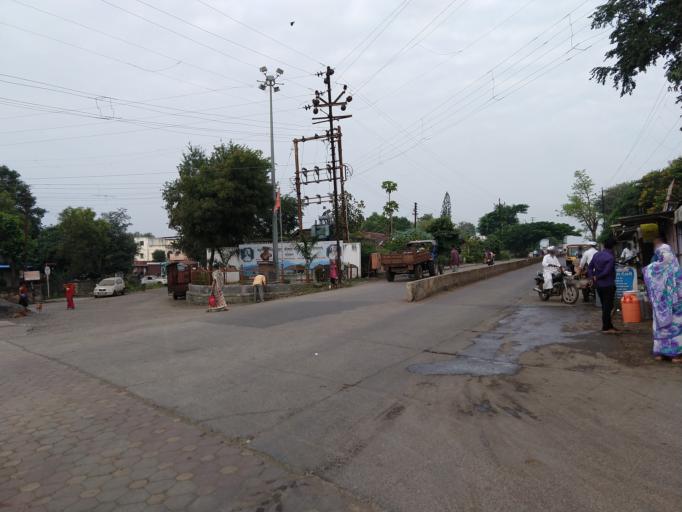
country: IN
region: Maharashtra
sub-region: Pune Division
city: Sasvad
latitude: 18.3465
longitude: 74.0281
